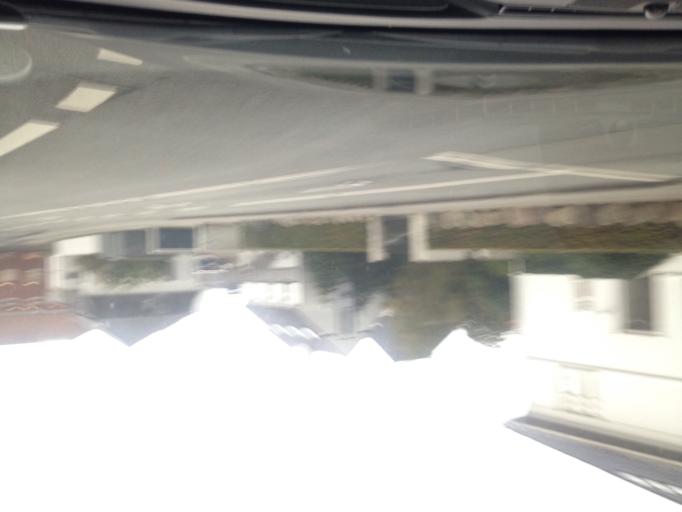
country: DK
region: South Denmark
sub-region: Kolding Kommune
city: Kolding
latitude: 55.4923
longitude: 9.4806
